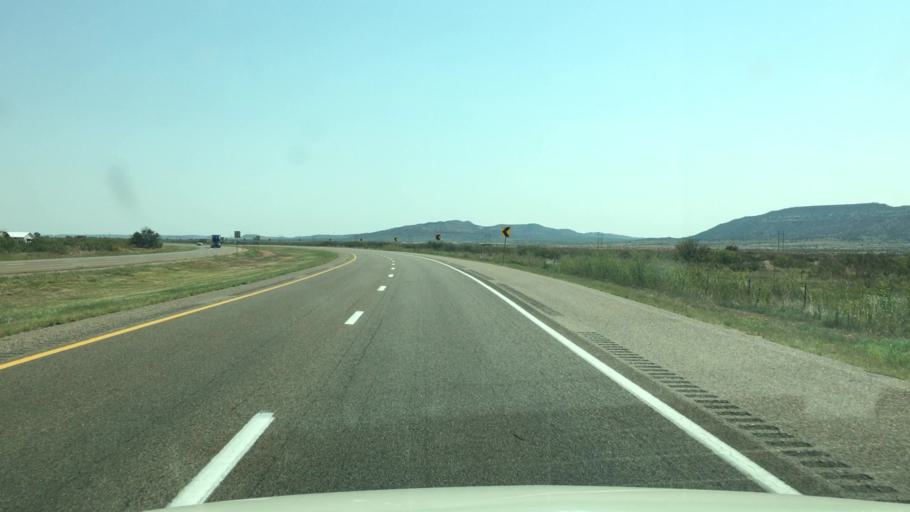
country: US
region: New Mexico
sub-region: Quay County
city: Tucumcari
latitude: 35.0936
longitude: -104.0652
